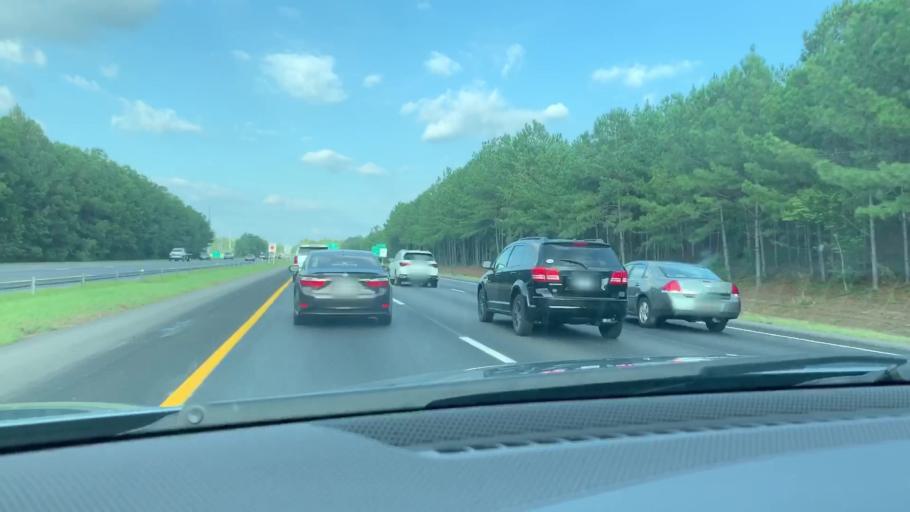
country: US
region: South Carolina
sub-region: Richland County
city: Woodfield
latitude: 34.0468
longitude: -80.9296
